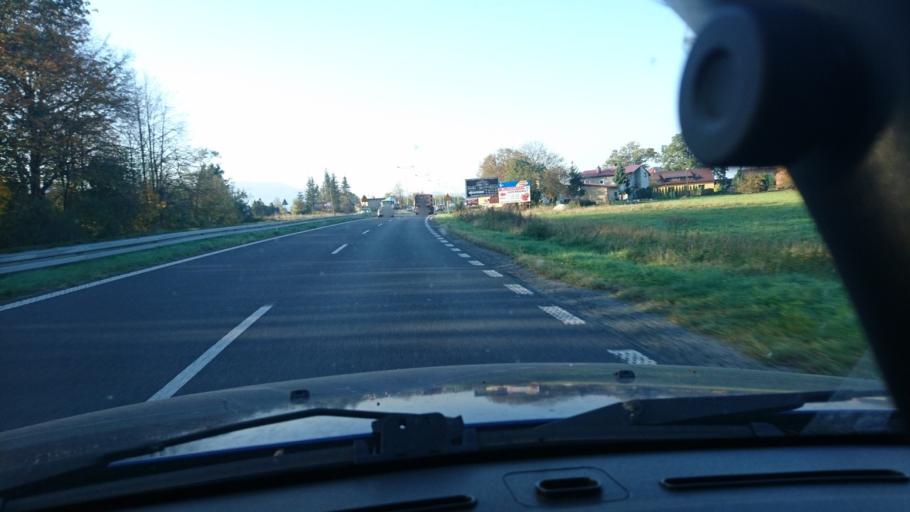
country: PL
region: Silesian Voivodeship
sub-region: Powiat cieszynski
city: Gorki Wielkie
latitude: 49.7618
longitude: 18.8081
